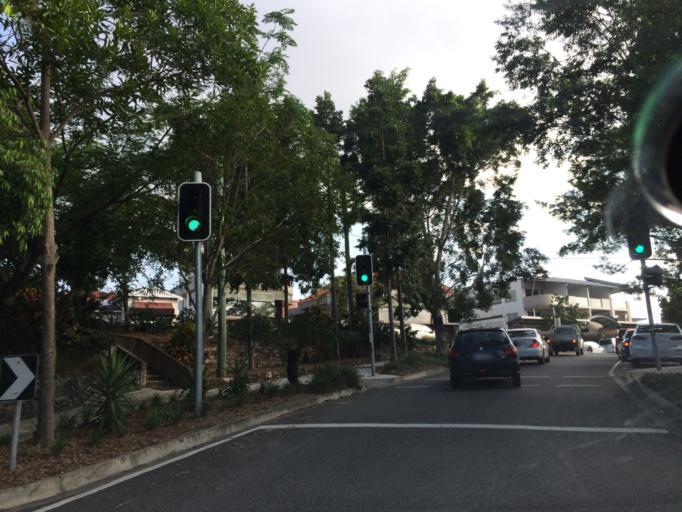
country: AU
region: Queensland
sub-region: Brisbane
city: Taringa
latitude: -27.4924
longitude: 152.9804
